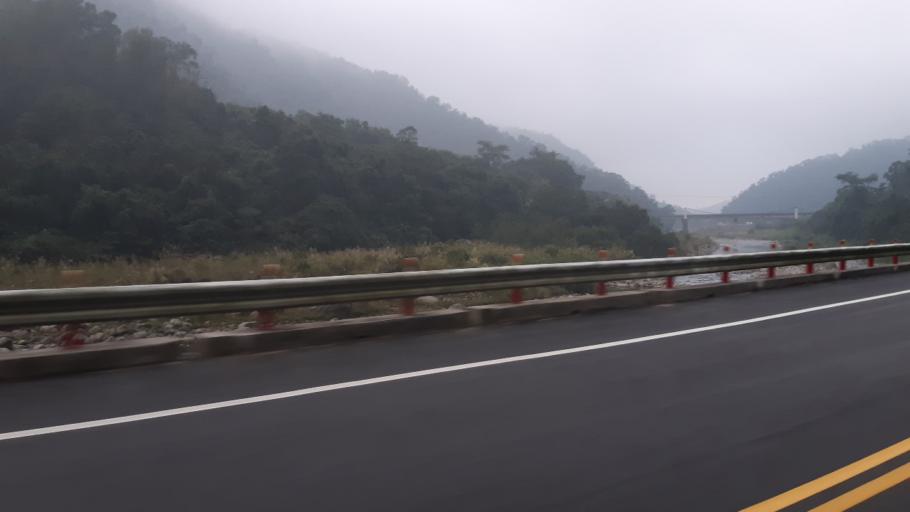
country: TW
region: Taiwan
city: Daxi
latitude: 24.7001
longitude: 121.1881
